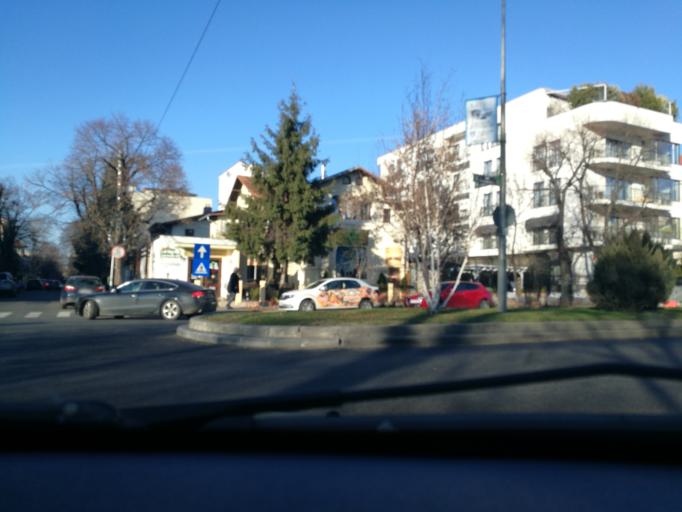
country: RO
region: Bucuresti
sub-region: Municipiul Bucuresti
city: Bucuresti
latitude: 44.4663
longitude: 26.0677
